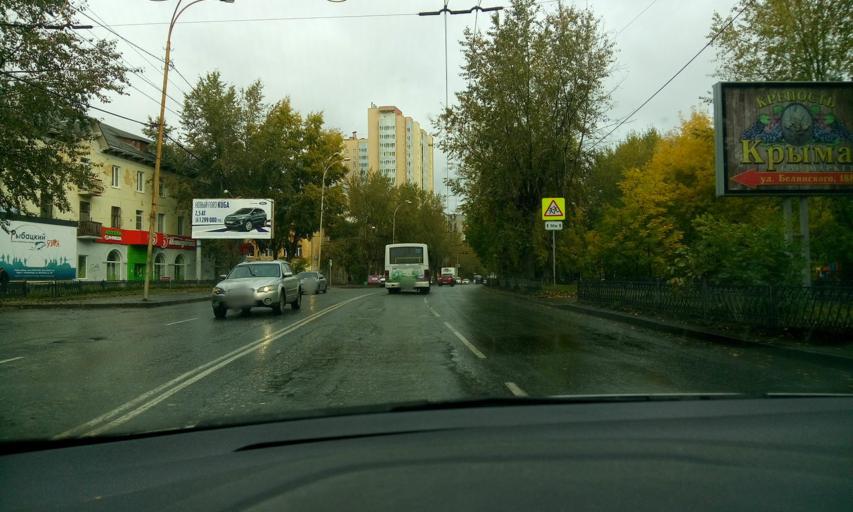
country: RU
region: Sverdlovsk
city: Yekaterinburg
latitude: 56.8062
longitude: 60.6249
